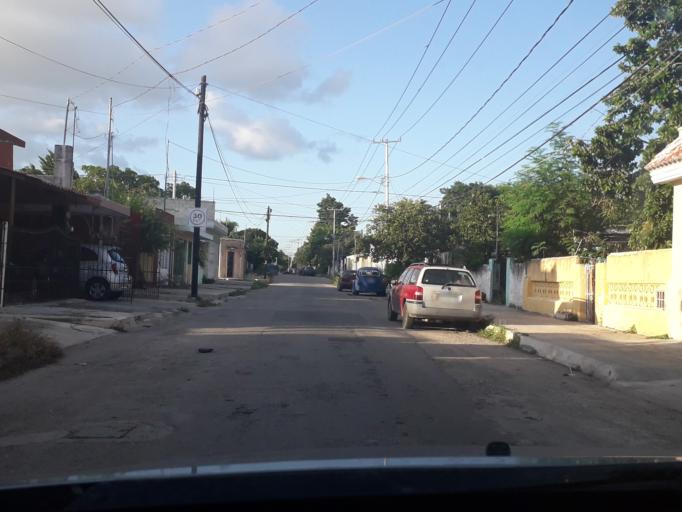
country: MX
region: Yucatan
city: Merida
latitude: 20.9742
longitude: -89.6465
